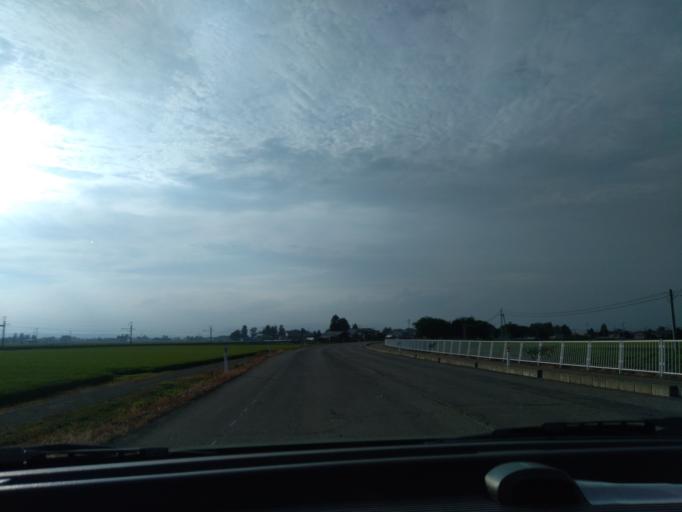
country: JP
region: Akita
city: Yokotemachi
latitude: 39.3801
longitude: 140.5319
